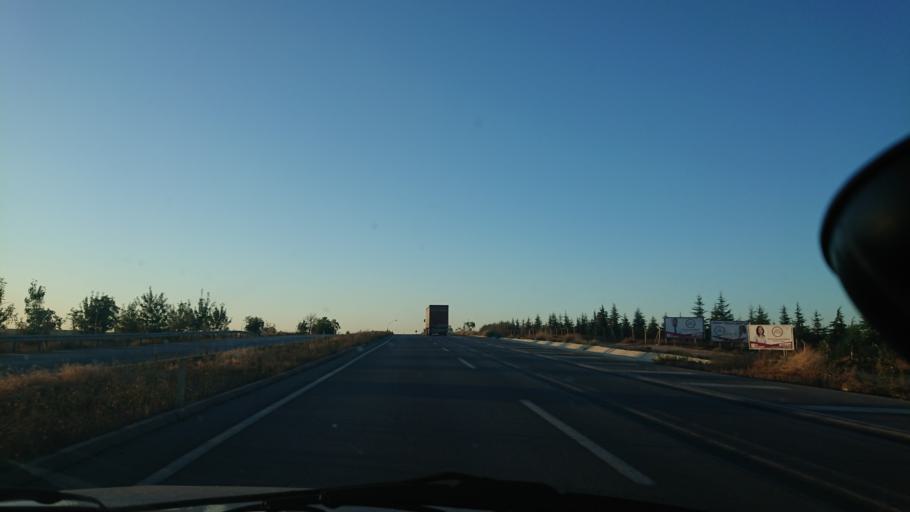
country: TR
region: Eskisehir
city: Mahmudiye
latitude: 39.4836
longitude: 30.9866
